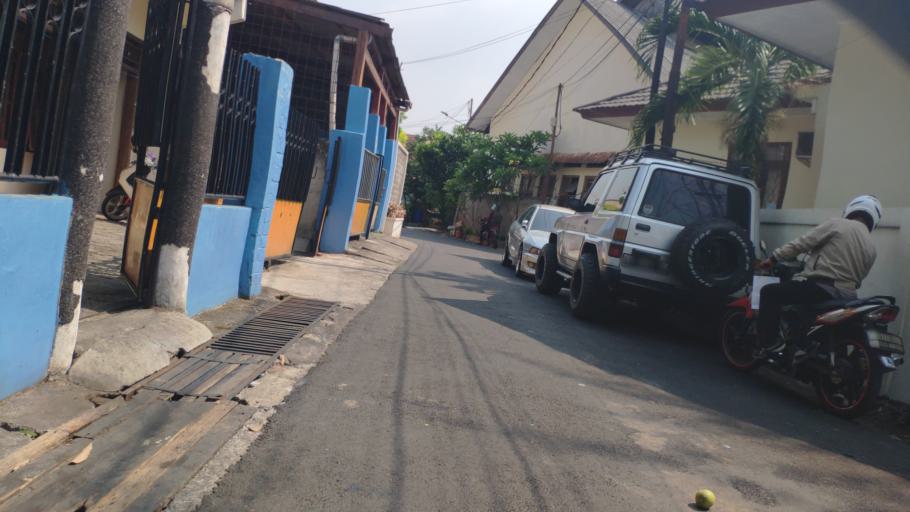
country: ID
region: Jakarta Raya
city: Jakarta
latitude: -6.2521
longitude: 106.7922
